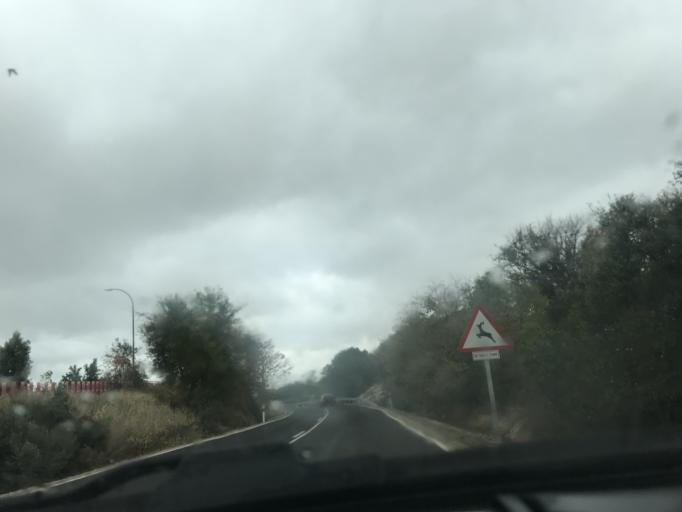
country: ES
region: Andalusia
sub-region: Provincia de Jaen
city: Peal de Becerro
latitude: 37.9170
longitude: -3.1077
